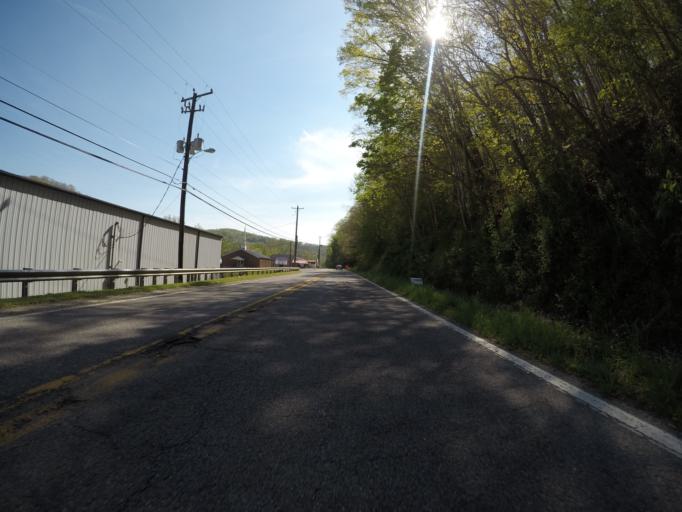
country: US
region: West Virginia
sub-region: Kanawha County
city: Clendenin
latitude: 38.4813
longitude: -81.3675
